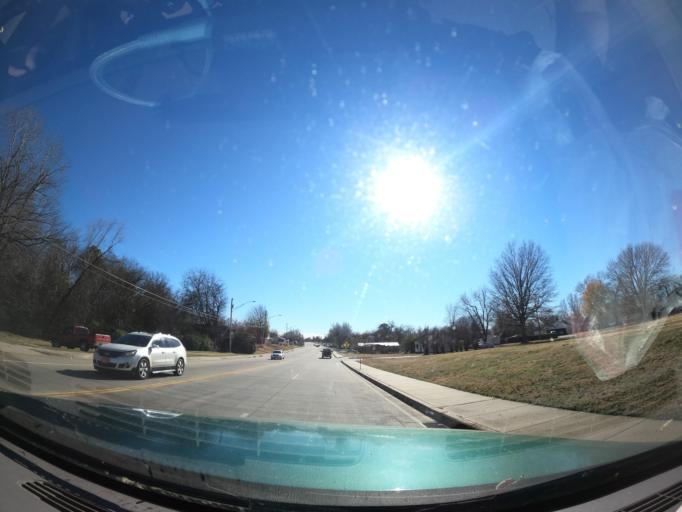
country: US
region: Oklahoma
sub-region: Wagoner County
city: Coweta
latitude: 35.9485
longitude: -95.6506
